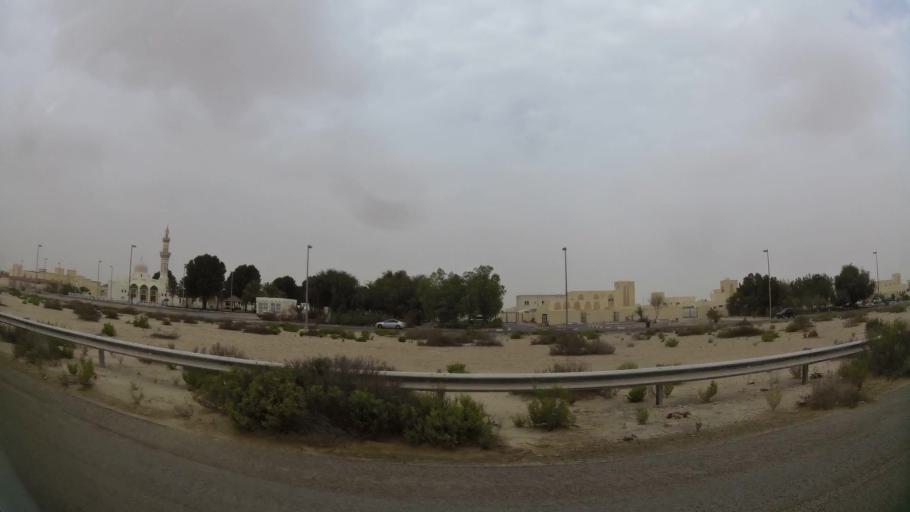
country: AE
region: Abu Dhabi
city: Abu Dhabi
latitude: 24.3977
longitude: 54.7469
